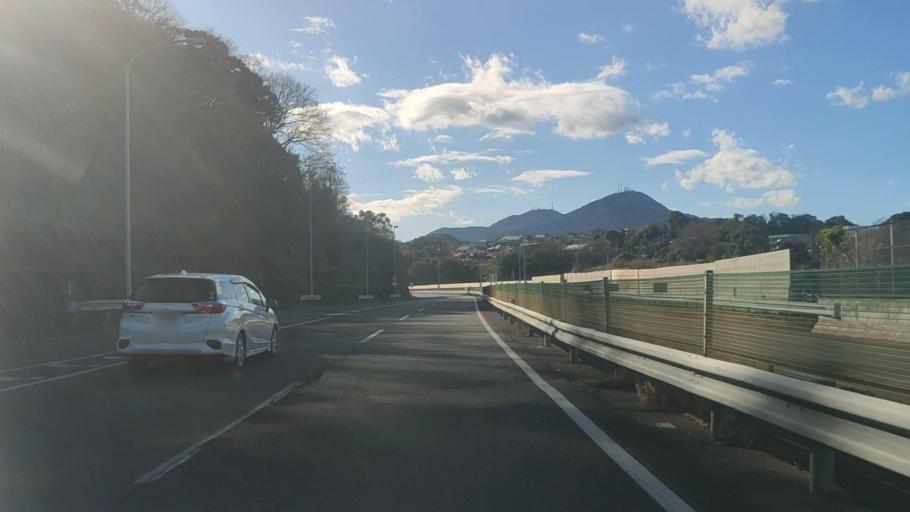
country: JP
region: Fukuoka
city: Kitakyushu
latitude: 33.8583
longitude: 130.8456
